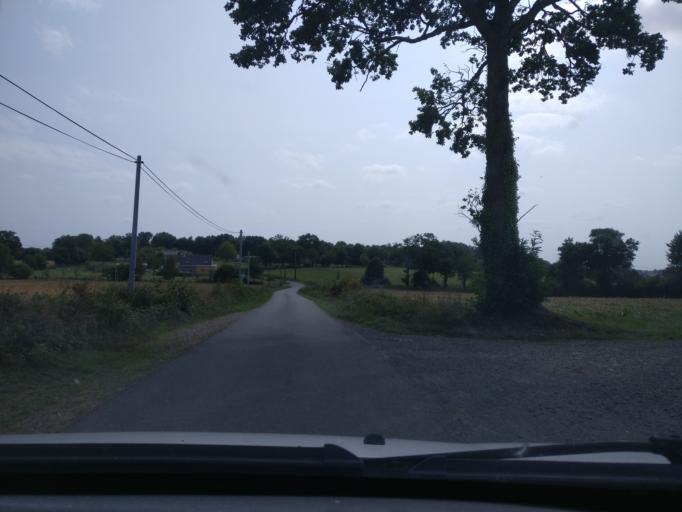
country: FR
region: Brittany
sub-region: Departement d'Ille-et-Vilaine
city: Erce-pres-Liffre
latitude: 48.2655
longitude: -1.5276
